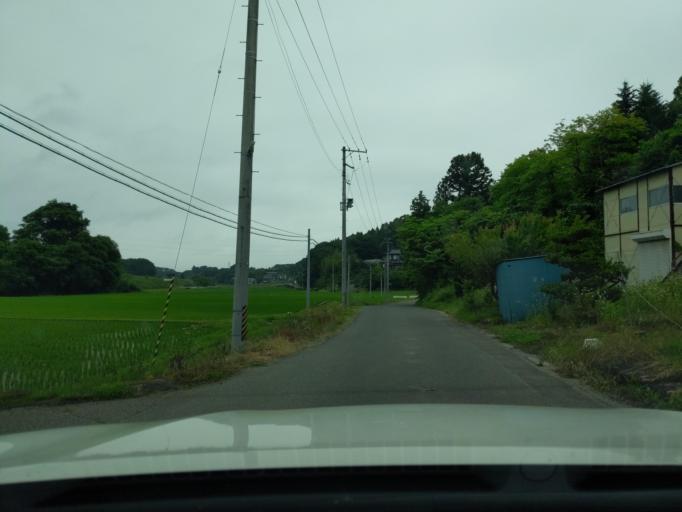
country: JP
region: Fukushima
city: Koriyama
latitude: 37.4010
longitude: 140.4253
